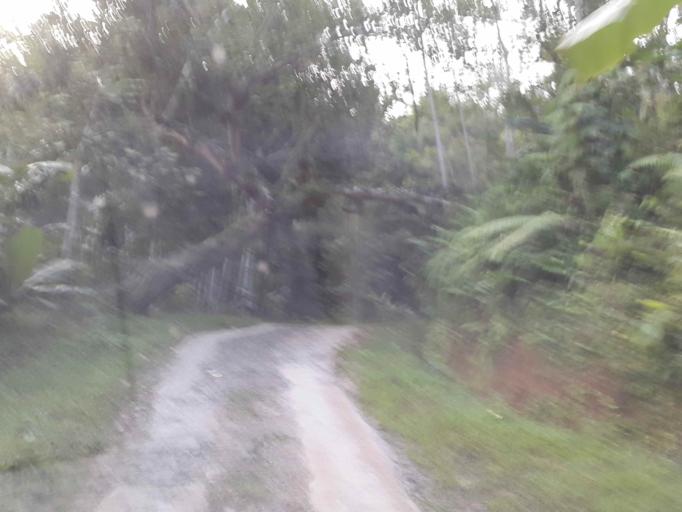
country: ID
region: West Java
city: Ciranjang-hilir
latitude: -6.8838
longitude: 107.2732
